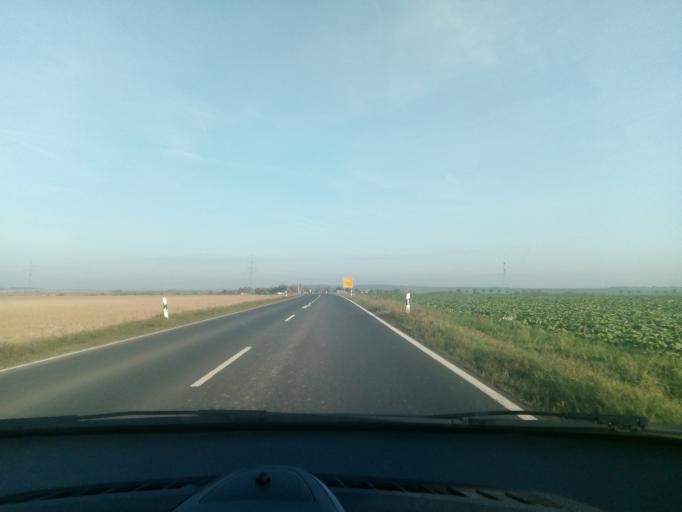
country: DE
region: Bavaria
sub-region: Regierungsbezirk Unterfranken
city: Oberpleichfeld
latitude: 49.8527
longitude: 10.0854
